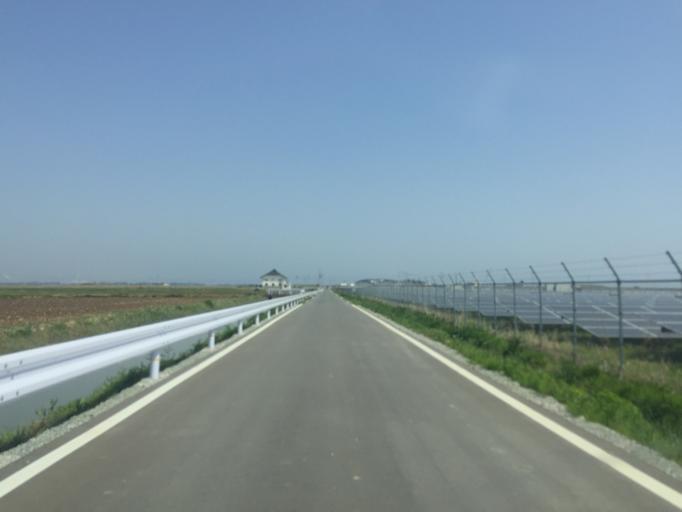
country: JP
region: Miyagi
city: Marumori
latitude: 37.7705
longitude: 140.9773
